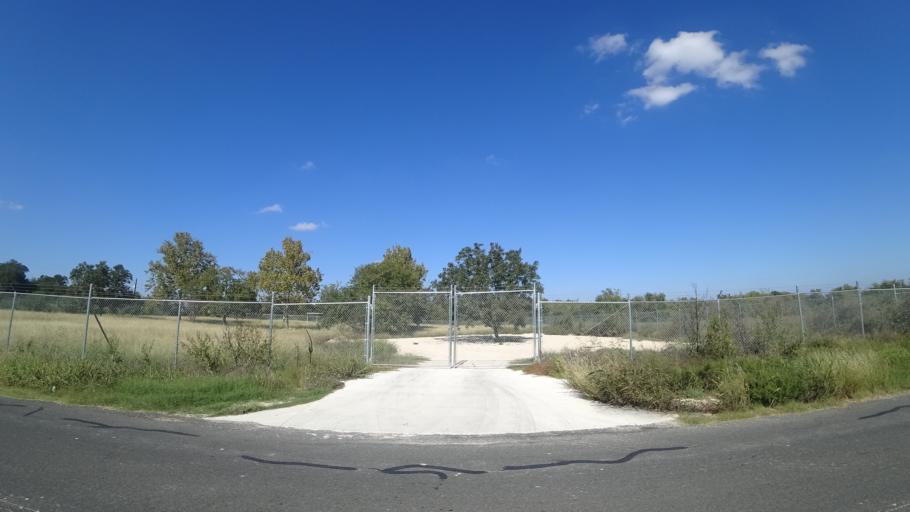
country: US
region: Texas
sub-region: Travis County
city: Manor
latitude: 30.3618
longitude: -97.6068
